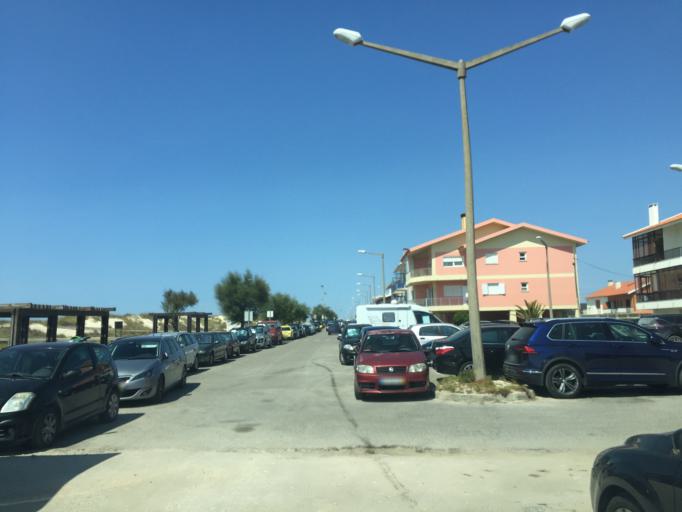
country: PT
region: Coimbra
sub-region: Mira
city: Mira
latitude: 40.3258
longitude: -8.8445
